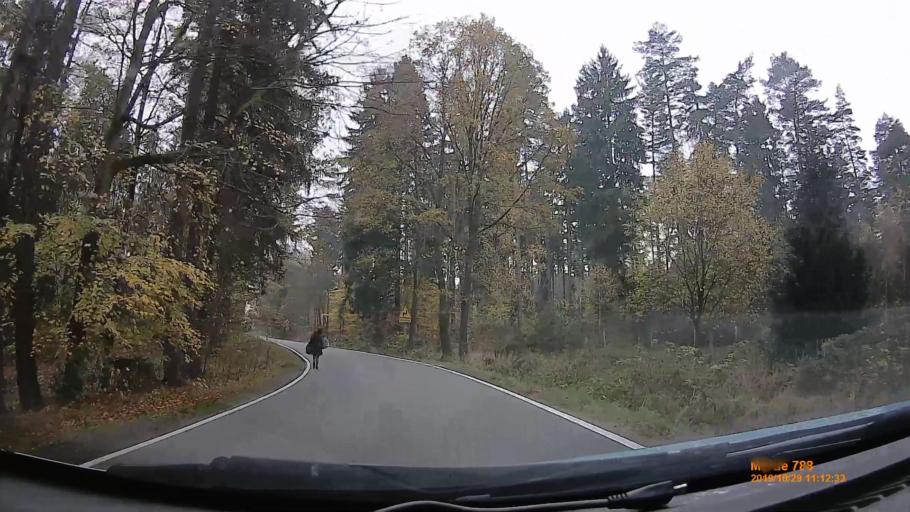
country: PL
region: Lower Silesian Voivodeship
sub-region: Powiat klodzki
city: Polanica-Zdroj
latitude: 50.4261
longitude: 16.5049
